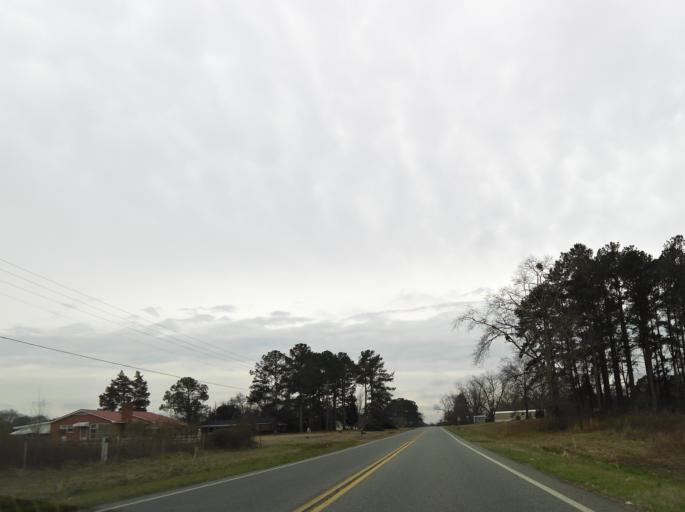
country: US
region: Georgia
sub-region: Bleckley County
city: Cochran
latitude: 32.4147
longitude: -83.3562
